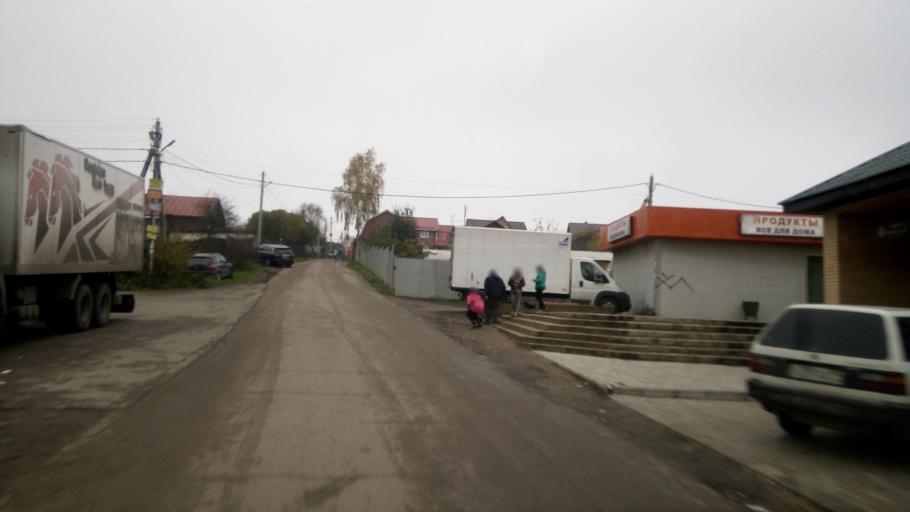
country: RU
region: Moskovskaya
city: Skhodnya
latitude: 55.9349
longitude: 37.2876
